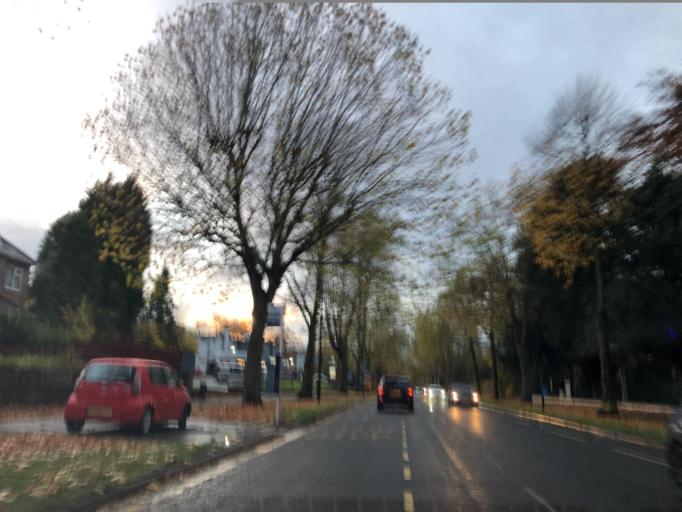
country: GB
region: England
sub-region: Coventry
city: Keresley
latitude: 52.4196
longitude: -1.5513
